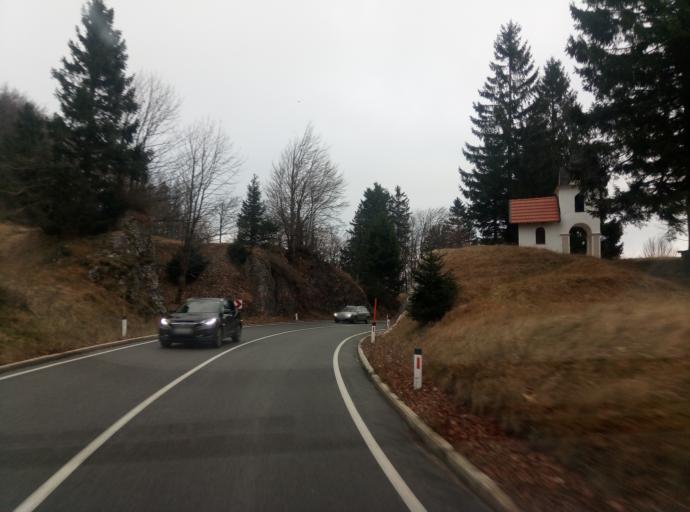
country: SI
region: Idrija
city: Idrija
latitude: 45.9231
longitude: 14.0350
